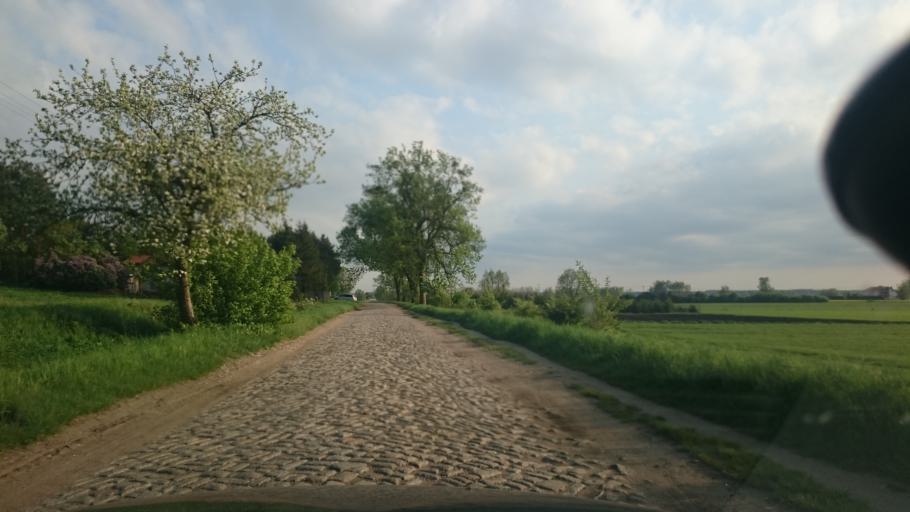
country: PL
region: Kujawsko-Pomorskie
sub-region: Grudziadz
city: Grudziadz
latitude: 53.4734
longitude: 18.8140
